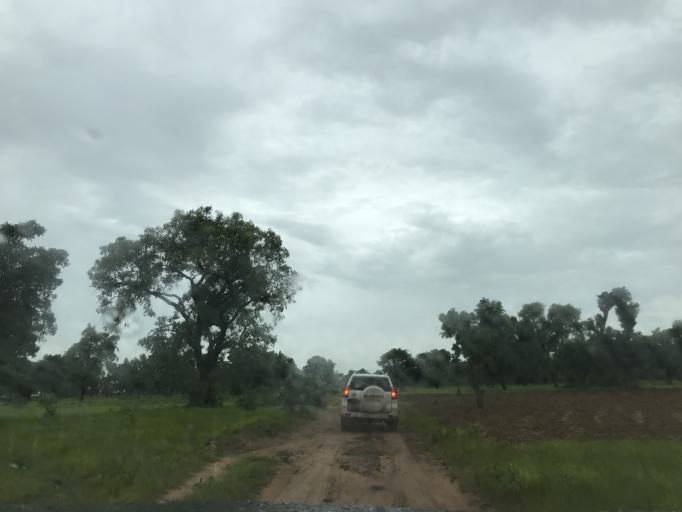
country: GH
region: Upper West
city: Wa
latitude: 10.5075
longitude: -2.7122
